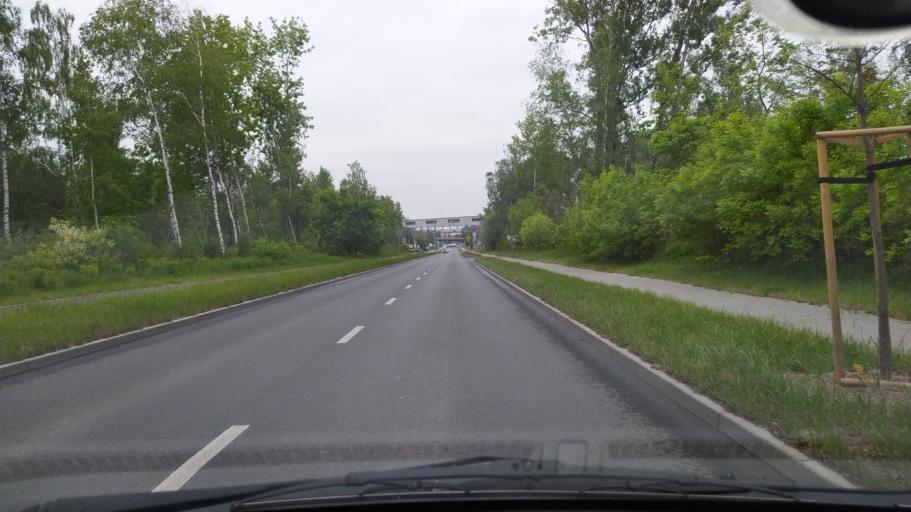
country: PL
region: Silesian Voivodeship
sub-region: Gliwice
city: Gliwice
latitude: 50.2773
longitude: 18.7099
